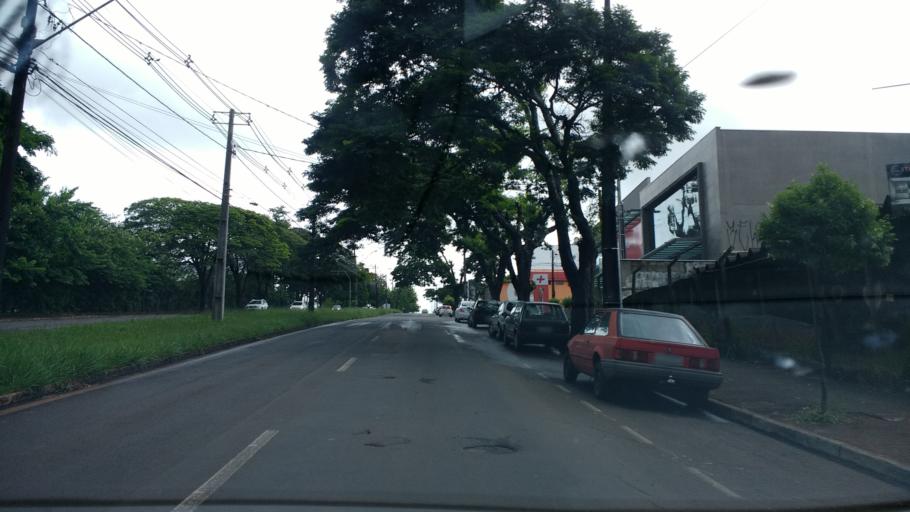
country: BR
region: Parana
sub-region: Londrina
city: Londrina
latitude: -23.3137
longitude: -51.2079
